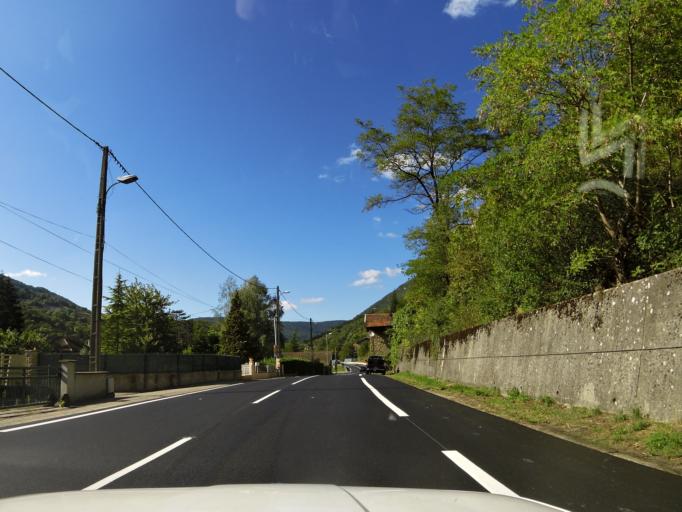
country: FR
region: Rhone-Alpes
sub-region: Departement de l'Ain
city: Tenay
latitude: 45.9282
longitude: 5.4950
